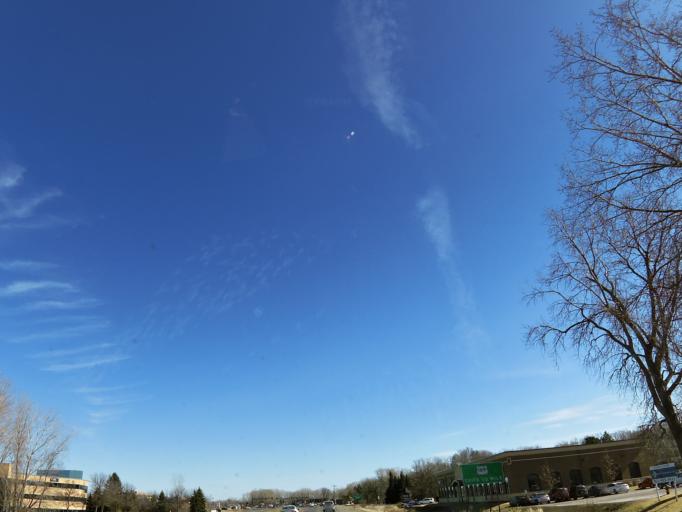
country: US
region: Minnesota
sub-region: Hennepin County
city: Plymouth
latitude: 44.9861
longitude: -93.4153
